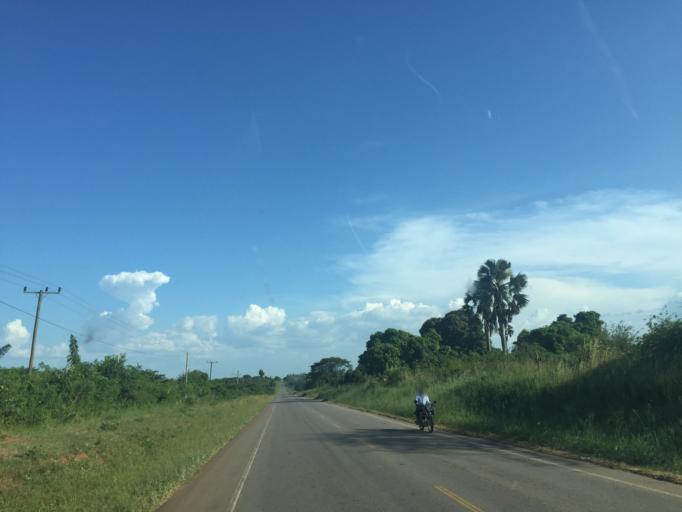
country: UG
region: Central Region
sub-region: Nakasongola District
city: Nakasongola
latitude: 1.2718
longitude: 32.4425
